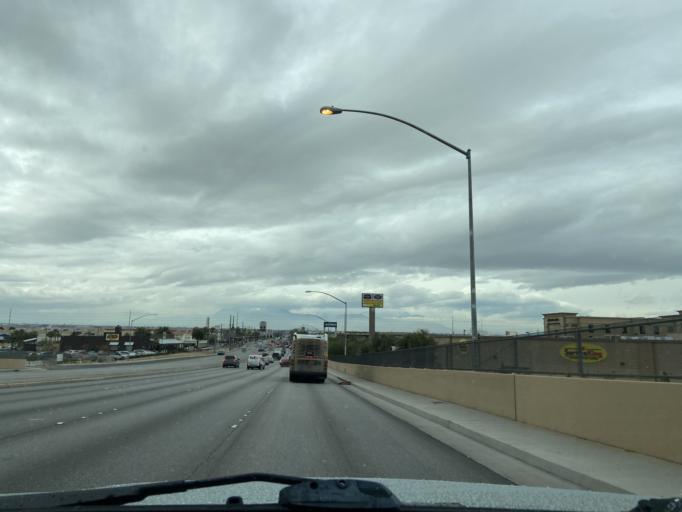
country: US
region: Nevada
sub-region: Clark County
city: North Las Vegas
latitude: 36.2402
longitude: -115.1086
